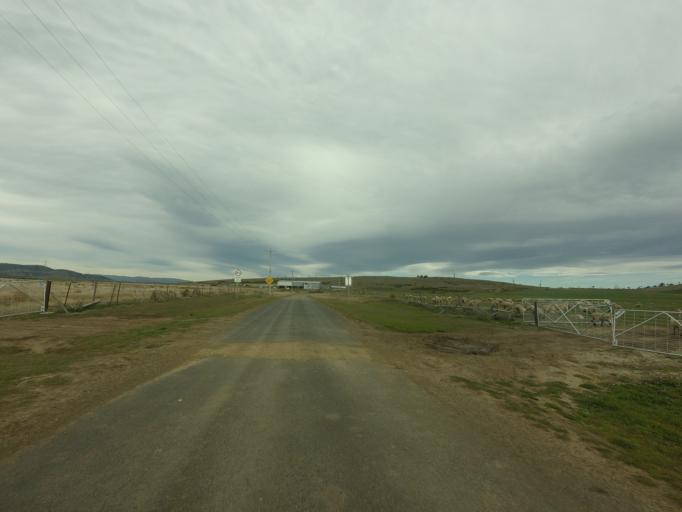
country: AU
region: Tasmania
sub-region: Derwent Valley
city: New Norfolk
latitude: -42.3847
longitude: 146.9855
